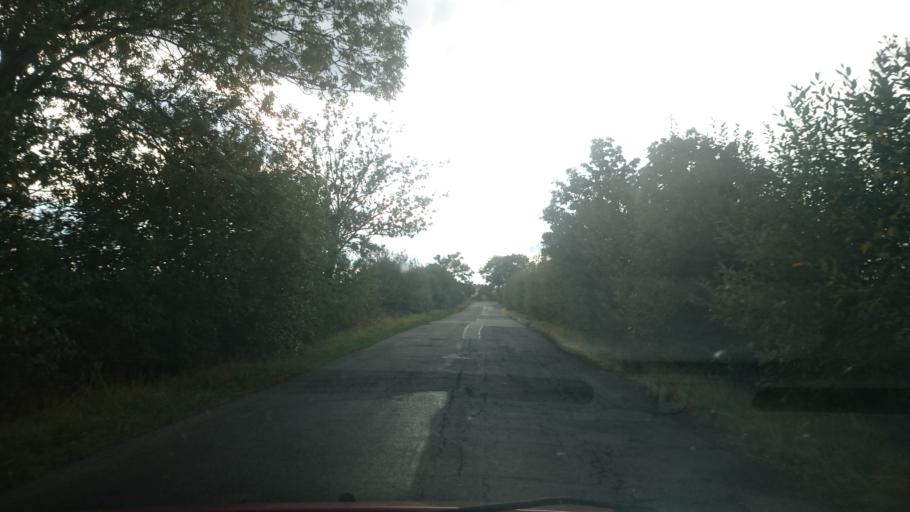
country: PL
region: Opole Voivodeship
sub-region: Powiat nyski
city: Otmuchow
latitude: 50.5002
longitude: 17.2067
